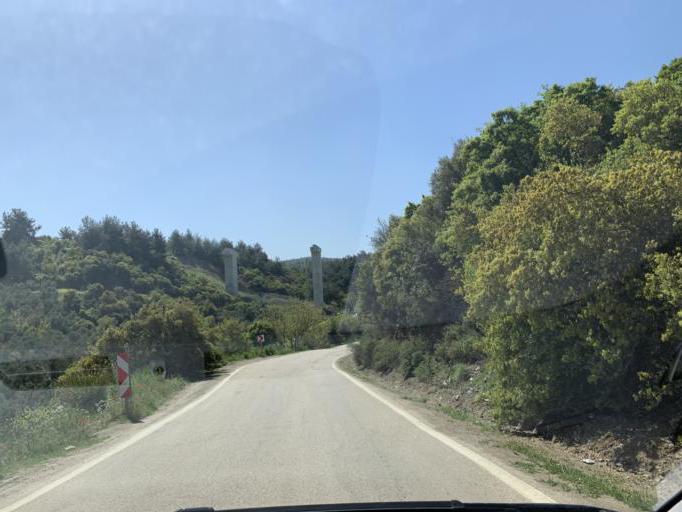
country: TR
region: Bursa
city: Niluefer
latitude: 40.3555
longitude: 28.9585
